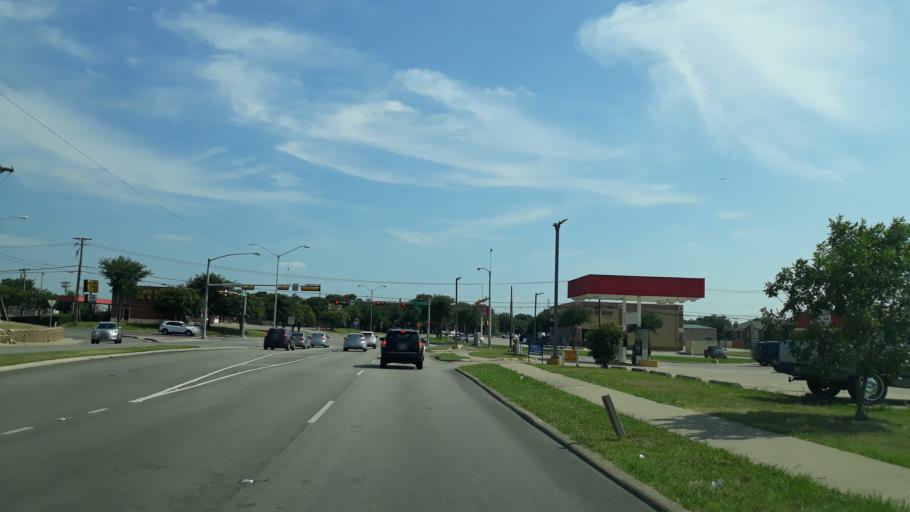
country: US
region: Texas
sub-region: Dallas County
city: Irving
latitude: 32.8340
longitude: -97.0097
